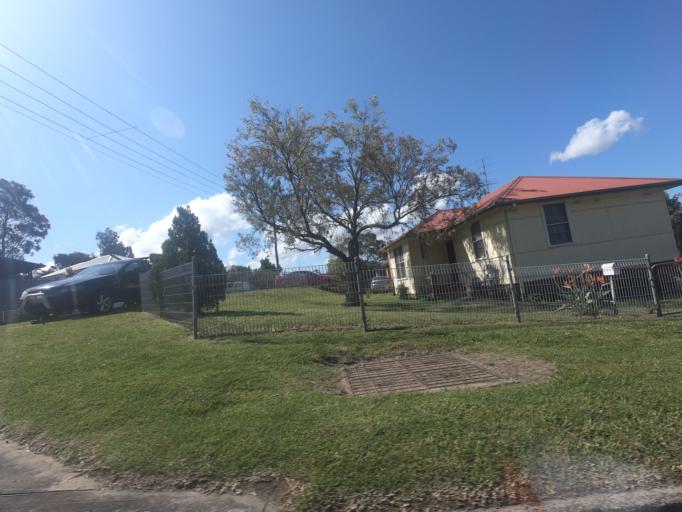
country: AU
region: New South Wales
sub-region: Wollongong
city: Cordeaux Heights
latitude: -34.4546
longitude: 150.8400
